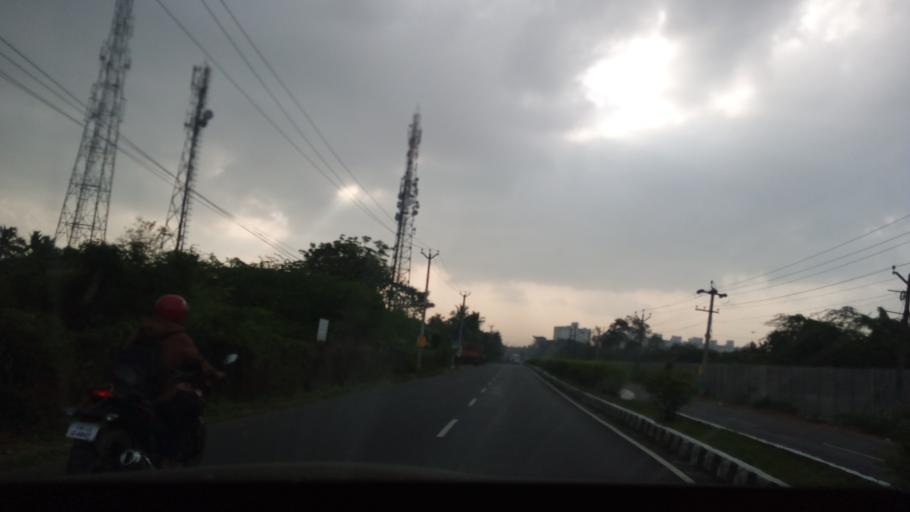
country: IN
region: Tamil Nadu
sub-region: Kancheepuram
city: Vengavasal
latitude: 12.8019
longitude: 80.1948
